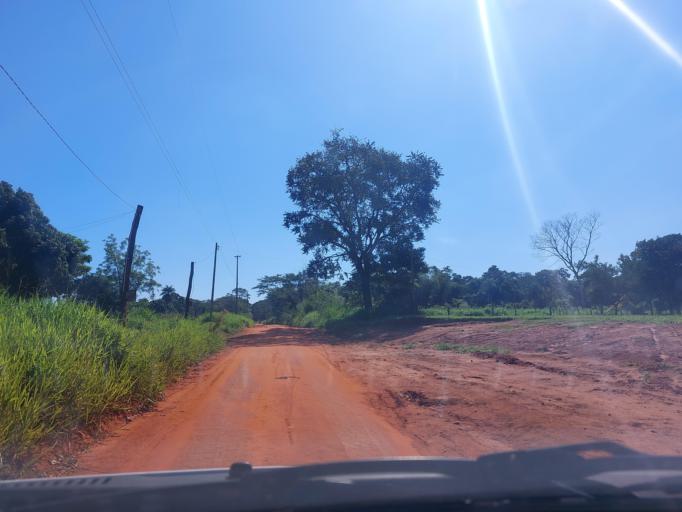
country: PY
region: San Pedro
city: Lima
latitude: -24.1600
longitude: -56.0115
